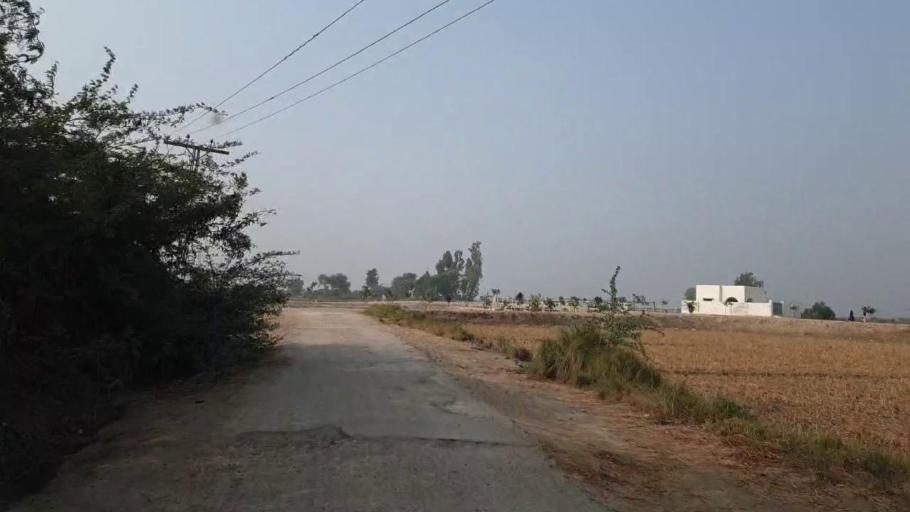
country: PK
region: Sindh
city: Tando Muhammad Khan
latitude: 25.0883
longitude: 68.5823
